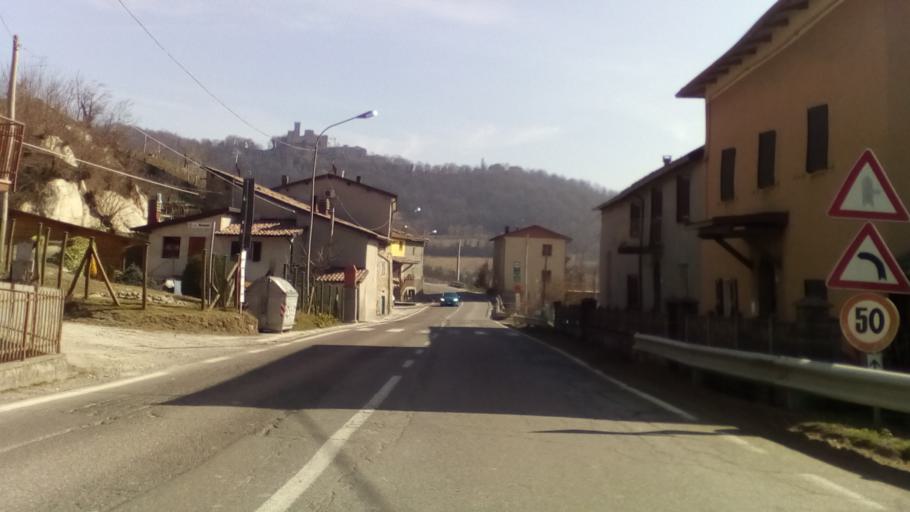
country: IT
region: Emilia-Romagna
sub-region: Provincia di Modena
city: Pavullo nel Frignano
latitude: 44.3151
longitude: 10.8003
